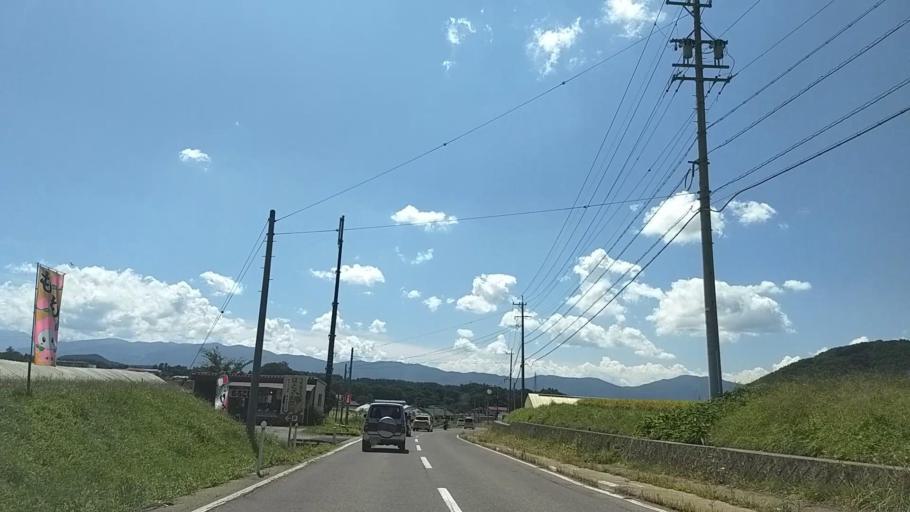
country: JP
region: Nagano
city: Chino
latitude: 36.0445
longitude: 138.2264
